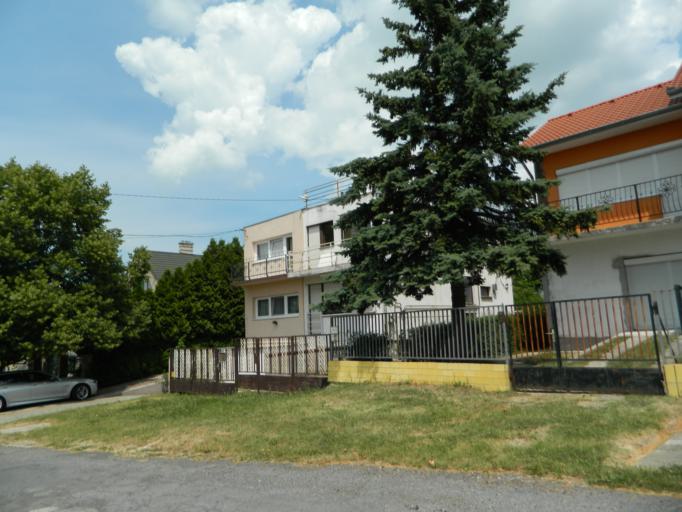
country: HU
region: Somogy
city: Balatonfoldvar
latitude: 46.8437
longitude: 17.8669
